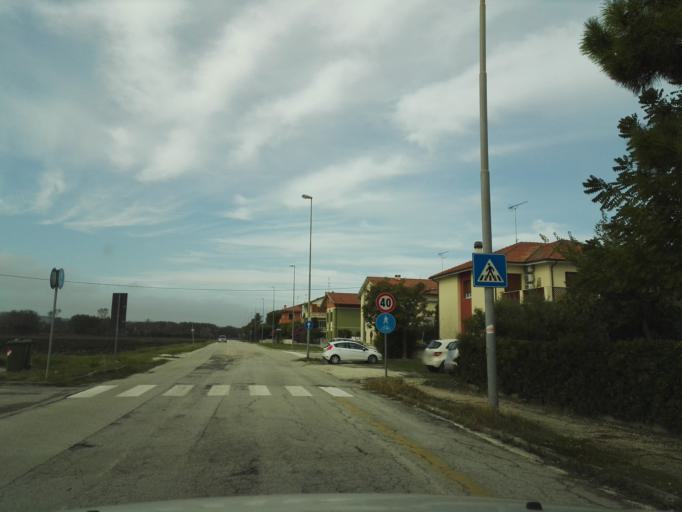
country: IT
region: The Marches
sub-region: Provincia di Pesaro e Urbino
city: Marotta
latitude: 43.7659
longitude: 13.1334
